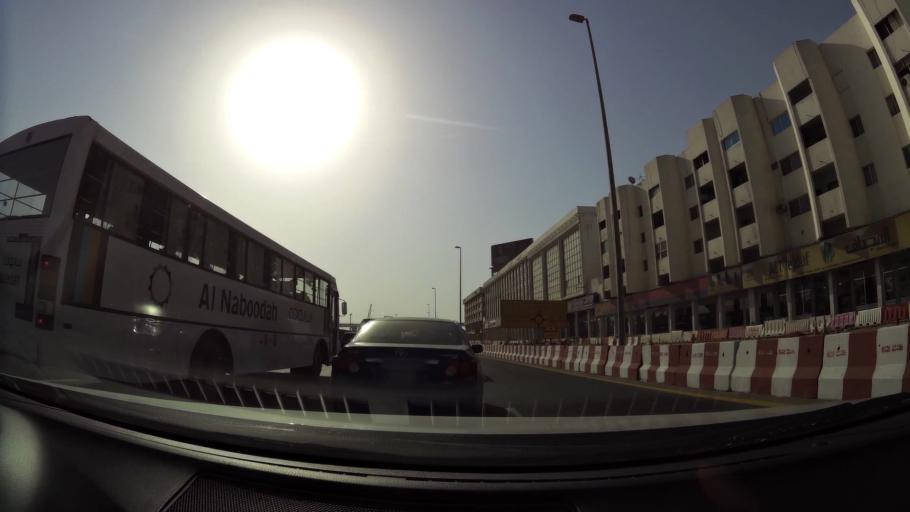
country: AE
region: Ash Shariqah
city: Sharjah
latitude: 25.2383
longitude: 55.2987
